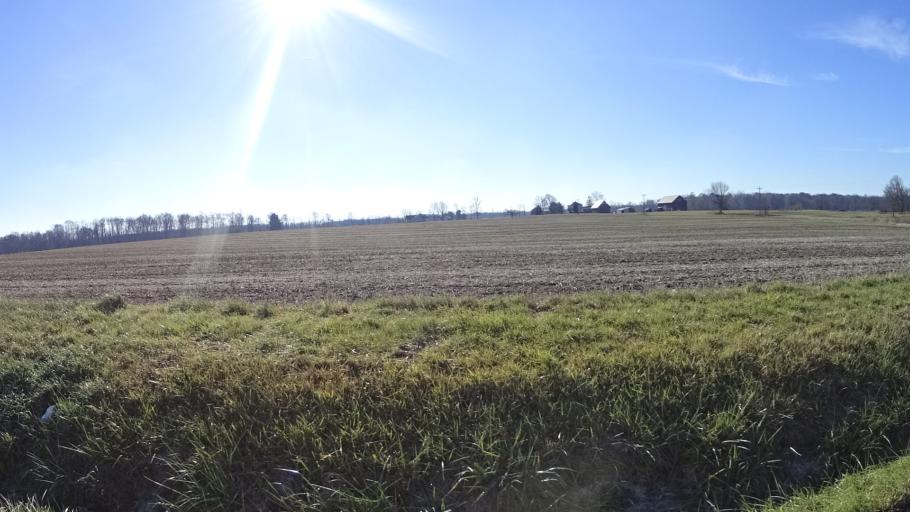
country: US
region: Ohio
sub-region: Huron County
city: New London
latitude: 41.1296
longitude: -82.3293
